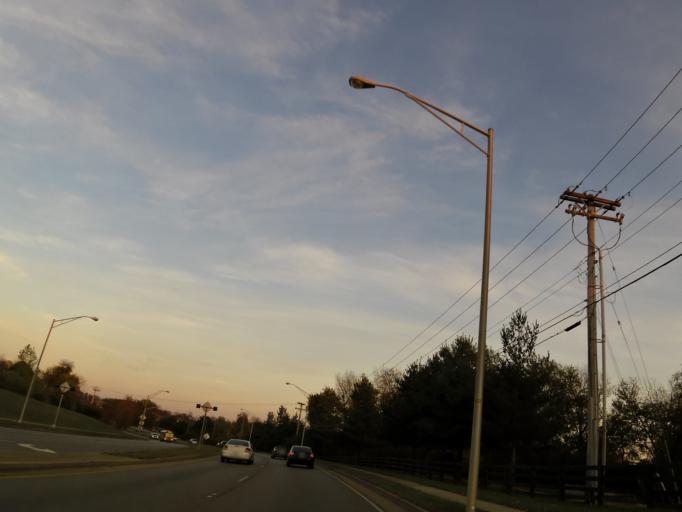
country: US
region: Kentucky
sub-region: Fayette County
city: Lexington
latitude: 37.9647
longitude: -84.4814
